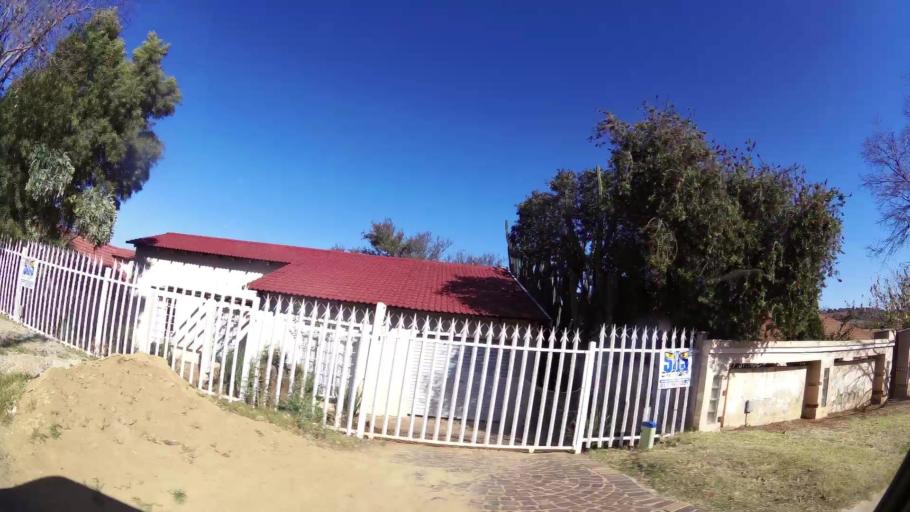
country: ZA
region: Gauteng
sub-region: City of Johannesburg Metropolitan Municipality
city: Johannesburg
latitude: -26.2760
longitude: 28.0310
